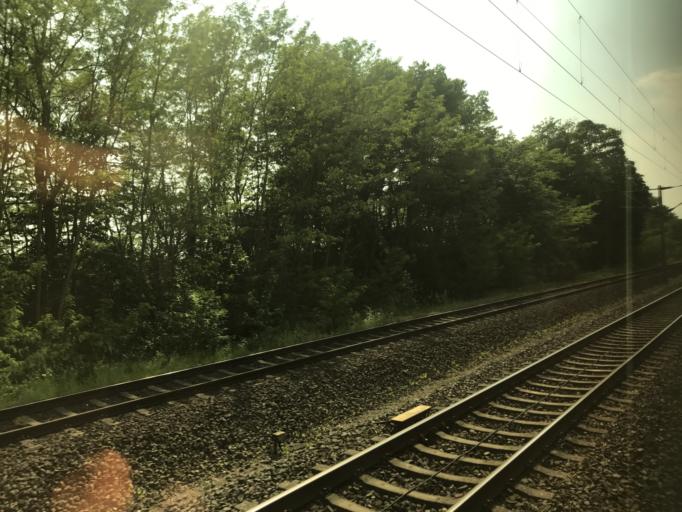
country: DE
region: Brandenburg
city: Nennhausen
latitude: 52.5996
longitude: 12.5094
